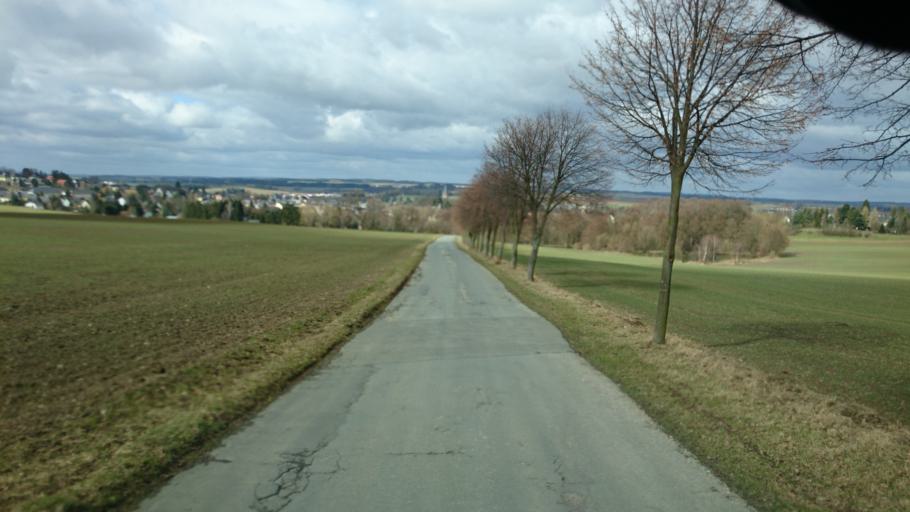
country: DE
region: Thuringia
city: Schleiz
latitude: 50.5688
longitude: 11.8236
